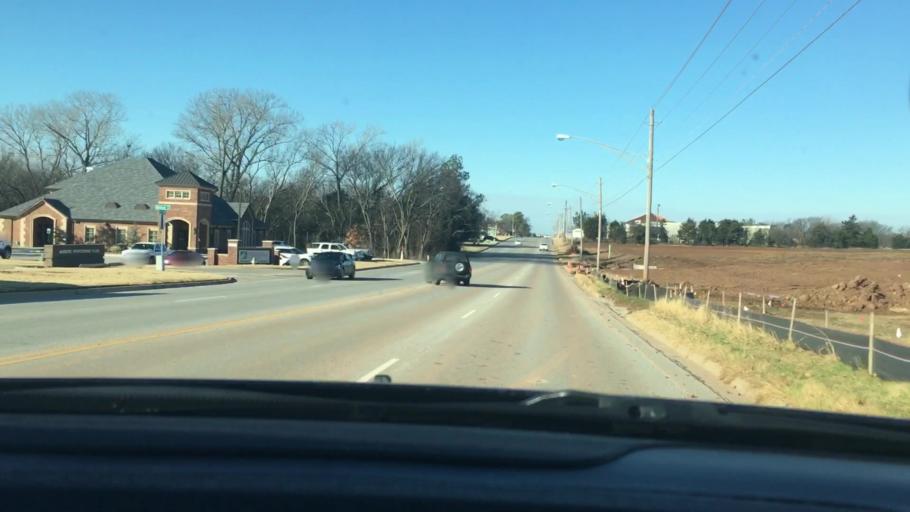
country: US
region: Oklahoma
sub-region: Carter County
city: Ardmore
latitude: 34.1876
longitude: -97.1486
